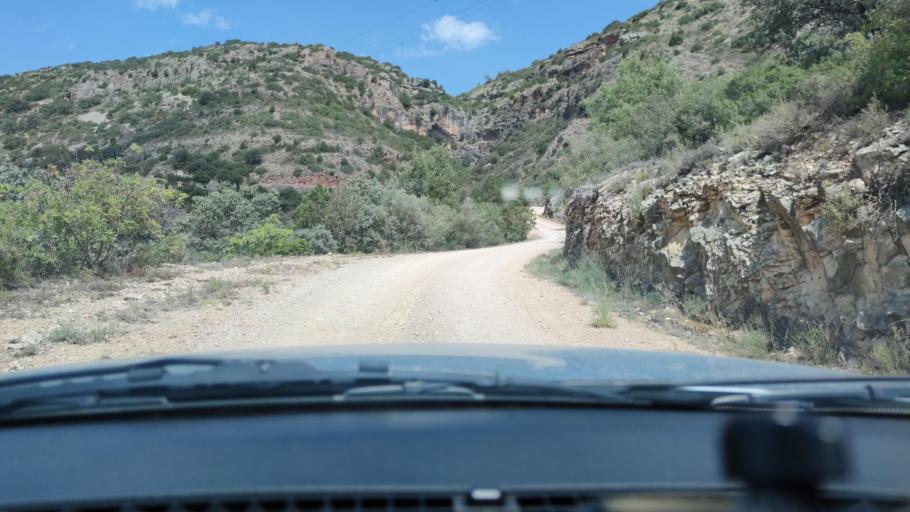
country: ES
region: Catalonia
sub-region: Provincia de Lleida
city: Camarasa
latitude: 41.9266
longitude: 0.8222
